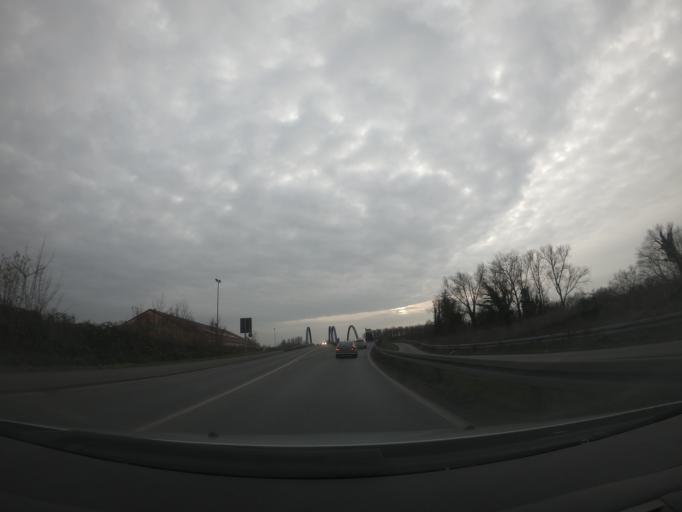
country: DE
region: North Rhine-Westphalia
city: Lunen
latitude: 51.6036
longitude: 7.4930
